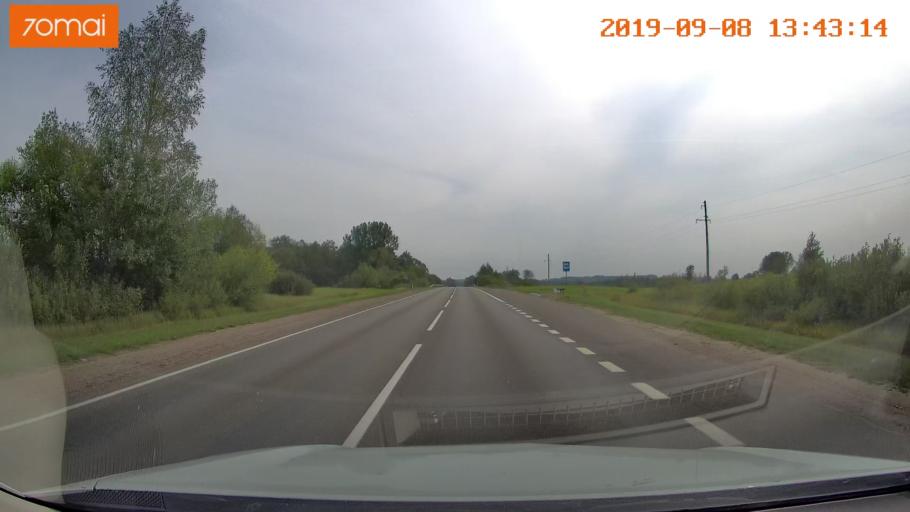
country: LT
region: Alytaus apskritis
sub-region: Alytus
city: Alytus
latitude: 54.3807
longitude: 24.1203
